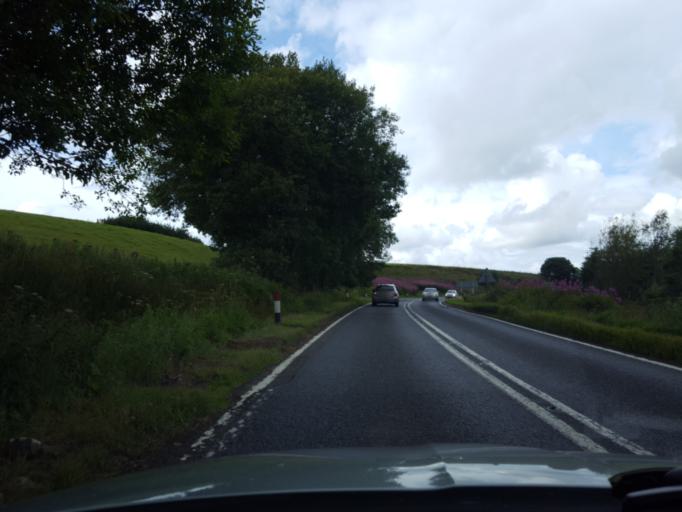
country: GB
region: Scotland
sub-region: Moray
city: Rothes
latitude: 57.4071
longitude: -3.3732
